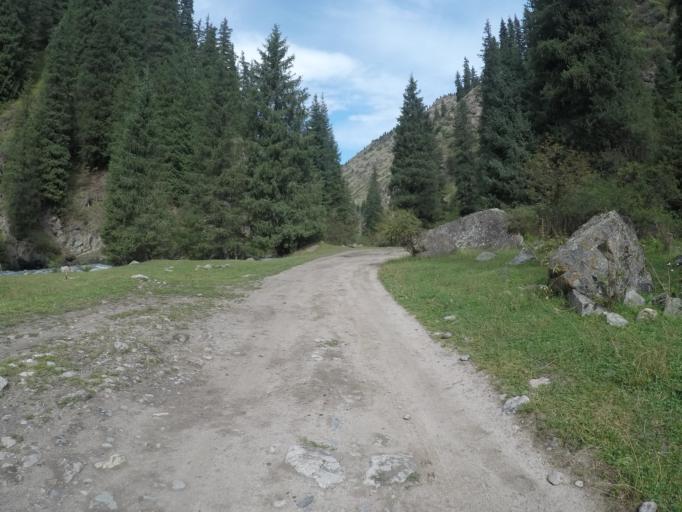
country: KG
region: Ysyk-Koel
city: Teploklyuchenka
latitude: 42.4375
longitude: 78.5602
